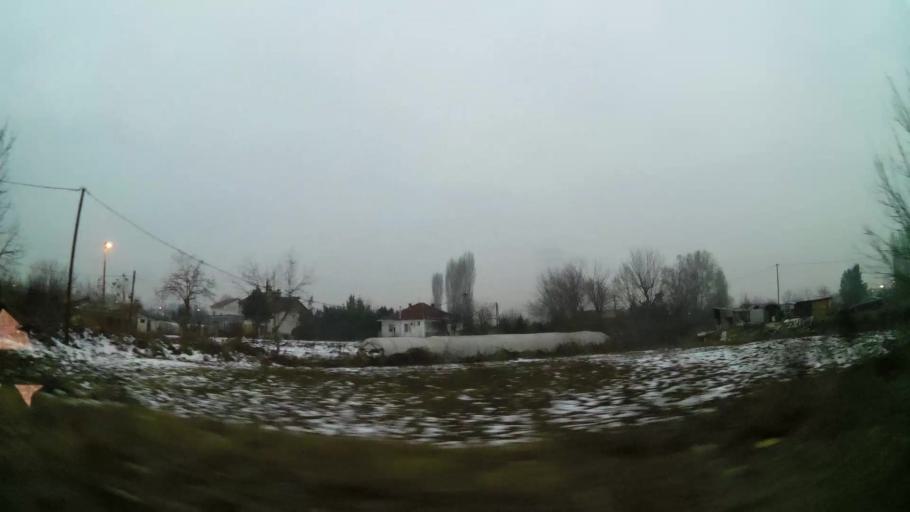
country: MK
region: Kisela Voda
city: Kisela Voda
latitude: 41.9715
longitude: 21.4919
